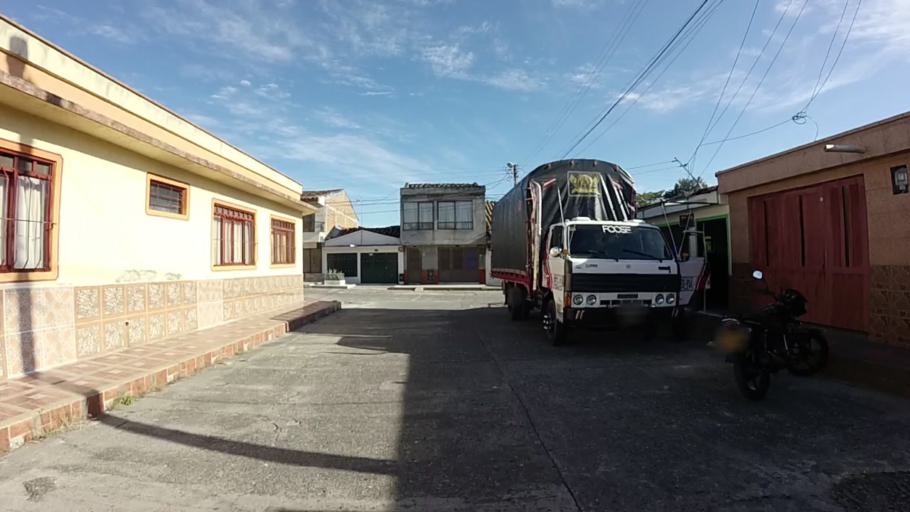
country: CO
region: Valle del Cauca
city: Cartago
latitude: 4.7539
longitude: -75.9223
